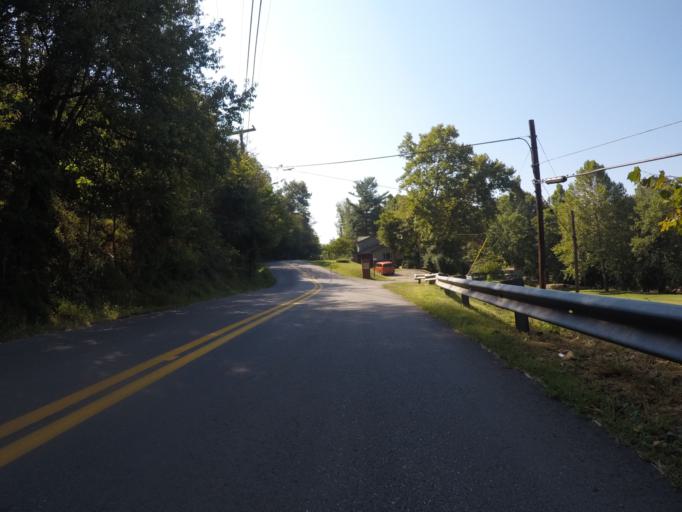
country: US
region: West Virginia
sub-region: Cabell County
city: Barboursville
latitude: 38.3821
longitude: -82.2836
